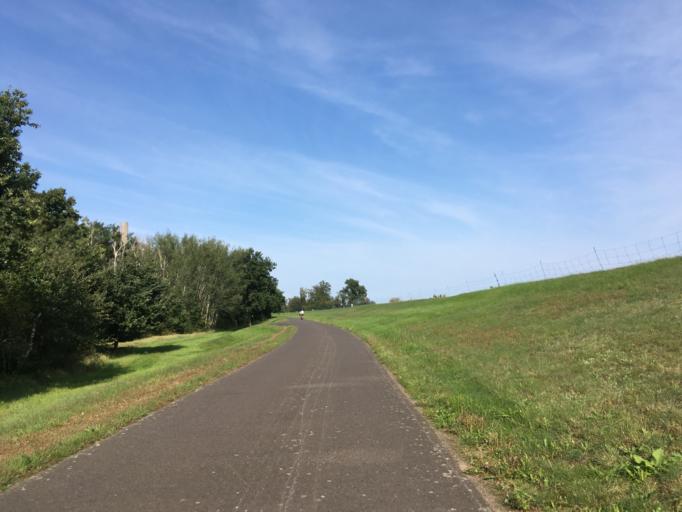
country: DE
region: Brandenburg
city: Vogelsang
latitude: 52.1623
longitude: 14.6977
